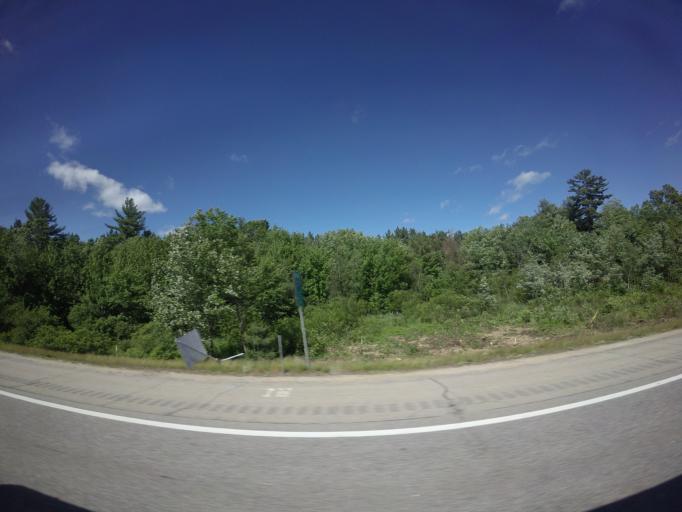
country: US
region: New Hampshire
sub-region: Rockingham County
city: Auburn
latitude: 42.9480
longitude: -71.3946
